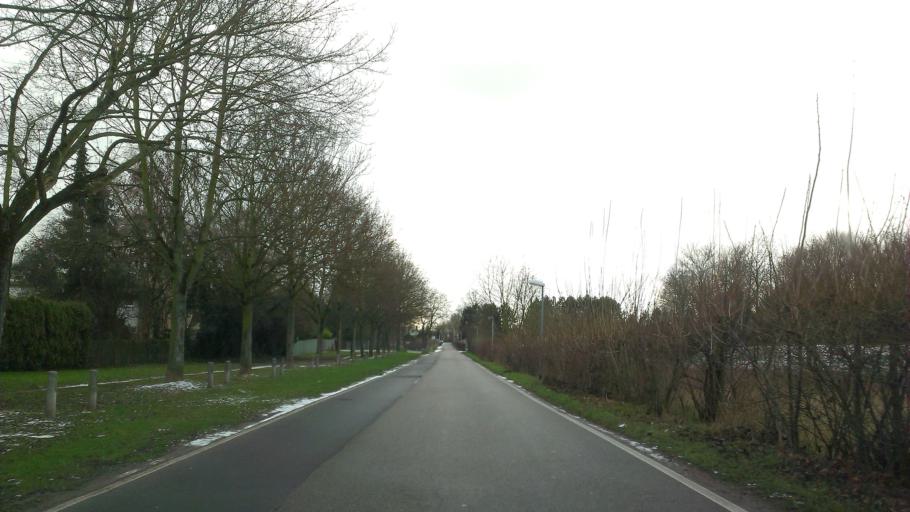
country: DE
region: Rheinland-Pfalz
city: Worms
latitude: 49.6314
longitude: 8.3398
